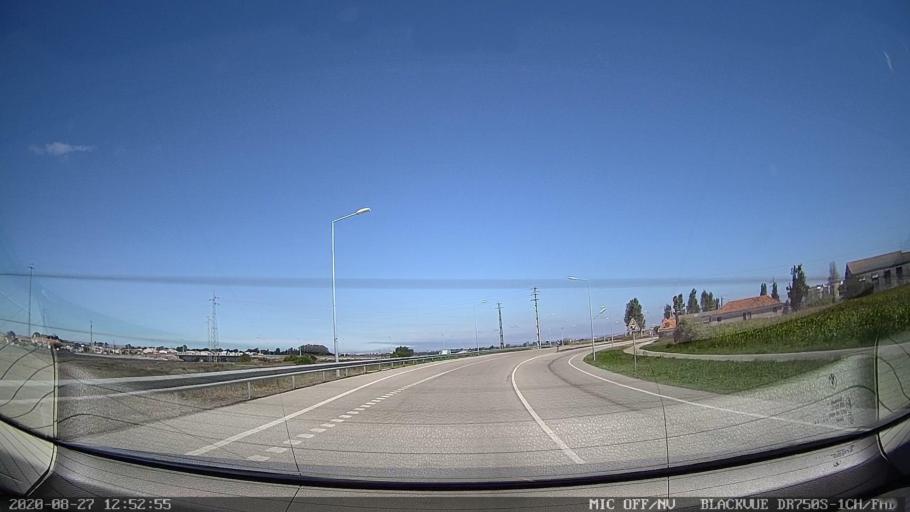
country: PT
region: Aveiro
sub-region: Ilhavo
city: Ilhavo
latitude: 40.6052
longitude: -8.6807
